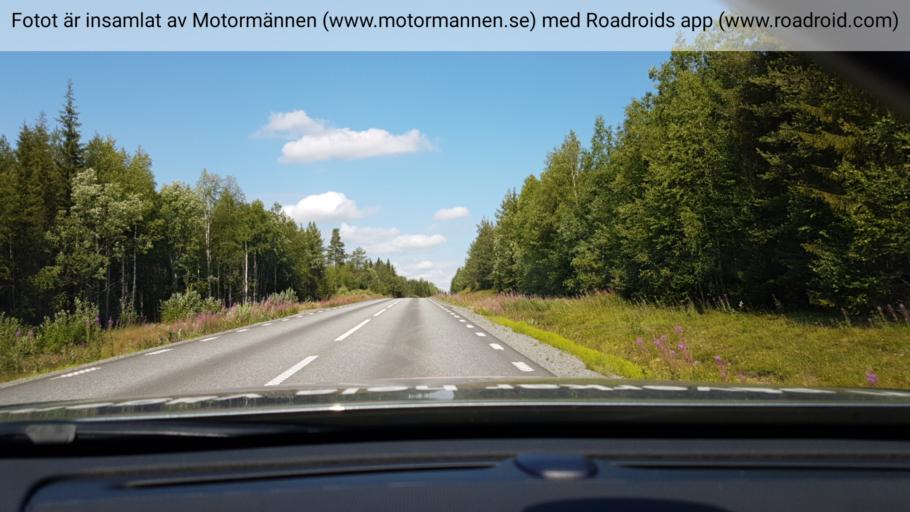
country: SE
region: Vaesterbotten
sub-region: Vilhelmina Kommun
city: Vilhelmina
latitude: 64.7111
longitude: 16.7069
